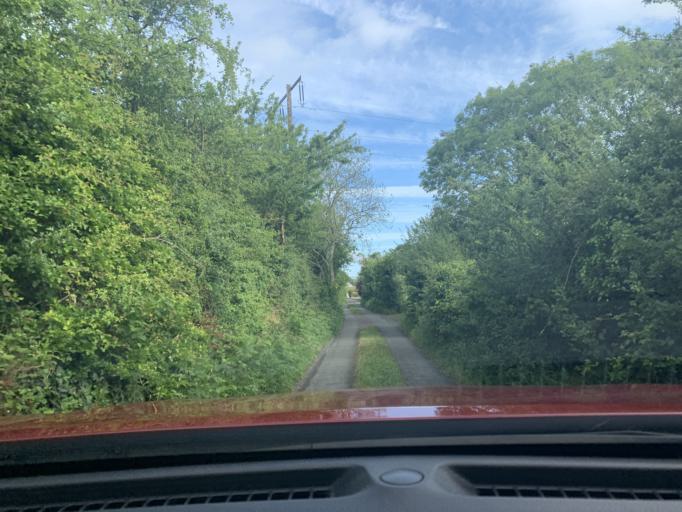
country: IE
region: Connaught
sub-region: Sligo
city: Sligo
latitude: 54.2324
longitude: -8.4664
